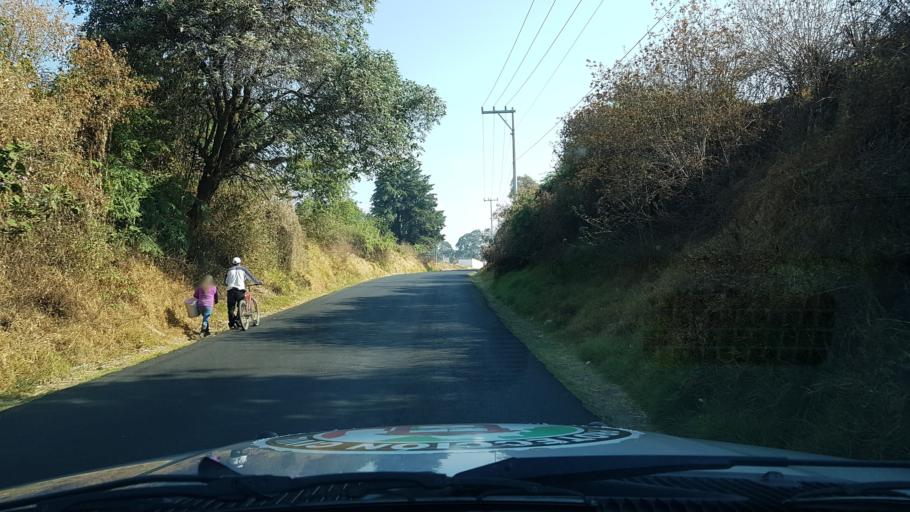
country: MX
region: Mexico
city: Atlautla
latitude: 19.0417
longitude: -98.7740
